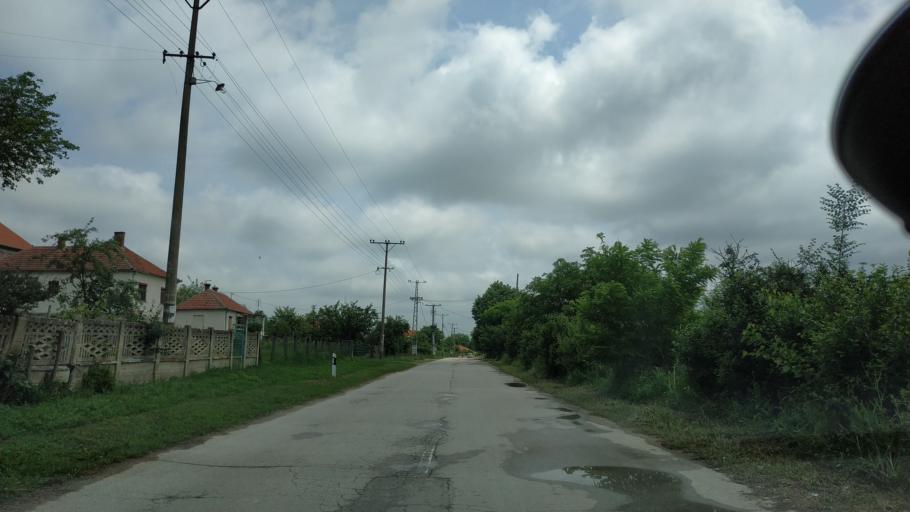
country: RS
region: Central Serbia
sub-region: Nisavski Okrug
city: Aleksinac
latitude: 43.4397
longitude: 21.7094
